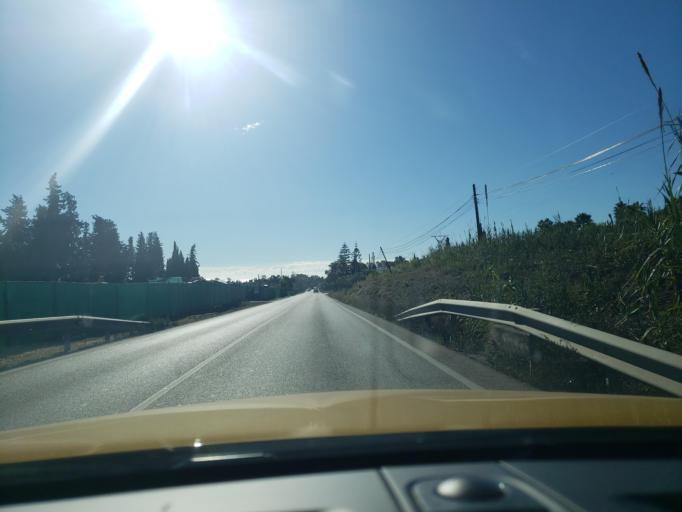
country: ES
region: Andalusia
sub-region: Provincia de Malaga
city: Benahavis
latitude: 36.4767
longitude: -5.0131
